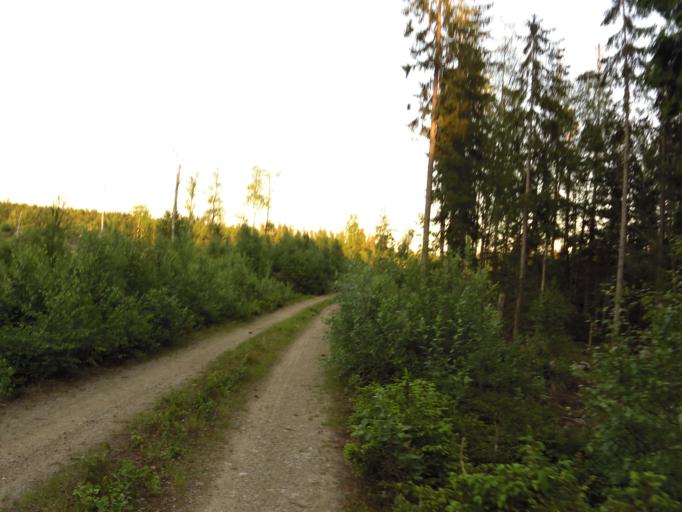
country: SE
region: Blekinge
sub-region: Olofstroms Kommun
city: Olofstroem
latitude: 56.4074
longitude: 14.5440
